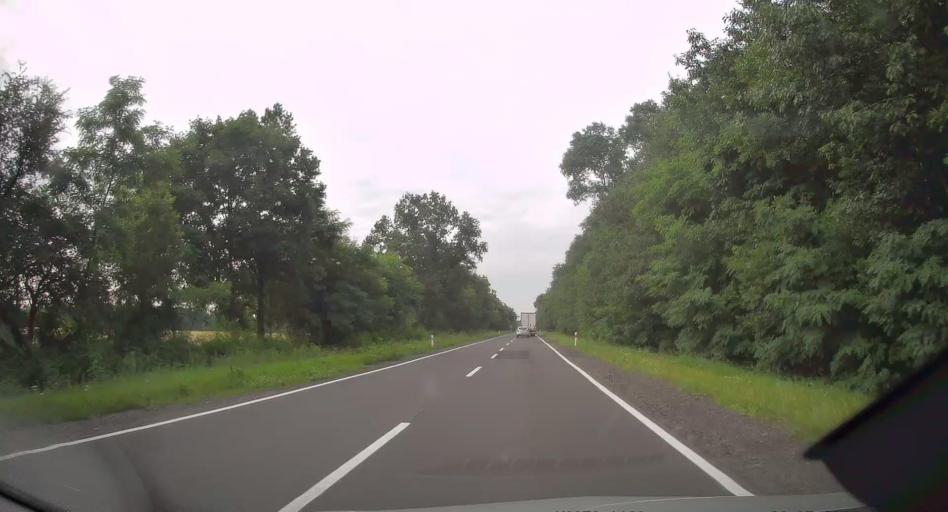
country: PL
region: Lodz Voivodeship
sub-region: Powiat radomszczanski
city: Plawno
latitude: 50.9672
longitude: 19.4066
